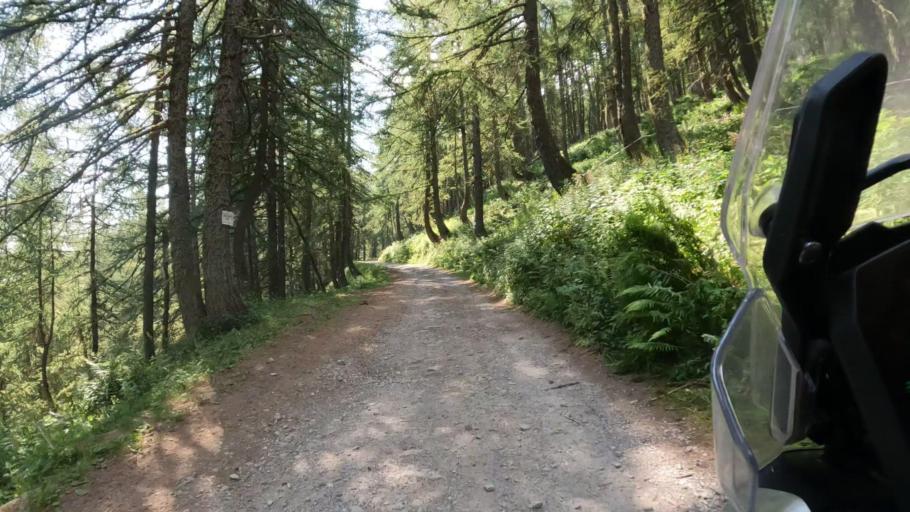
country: IT
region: Piedmont
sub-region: Provincia di Cuneo
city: Briga Alta
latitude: 44.0857
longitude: 7.7299
